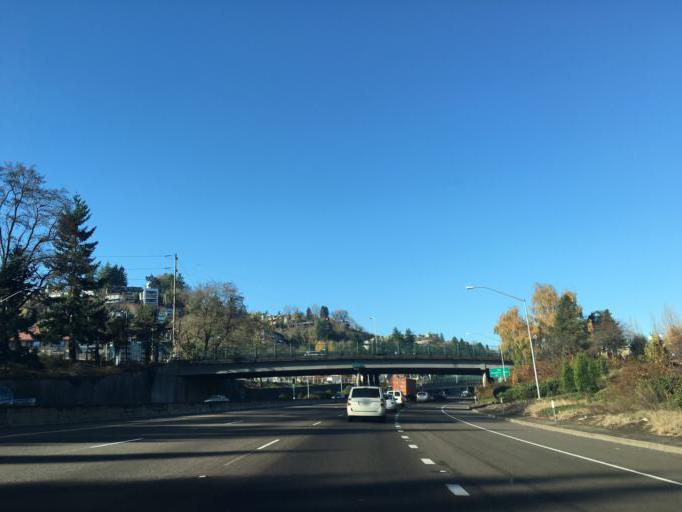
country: US
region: Oregon
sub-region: Multnomah County
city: Portland
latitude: 45.5058
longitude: -122.6804
